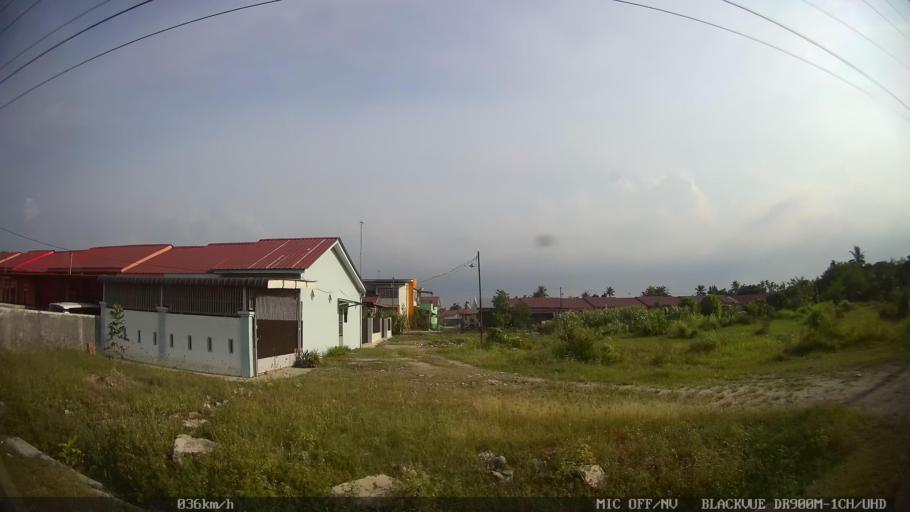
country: ID
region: North Sumatra
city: Binjai
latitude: 3.6209
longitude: 98.5223
